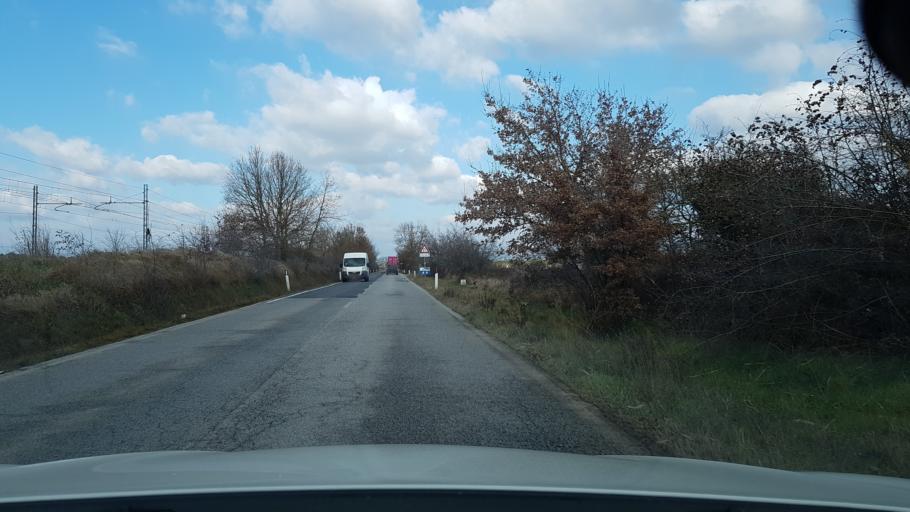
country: IT
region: Umbria
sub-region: Provincia di Perugia
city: Castiglione del Lago
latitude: 43.1386
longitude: 12.0258
